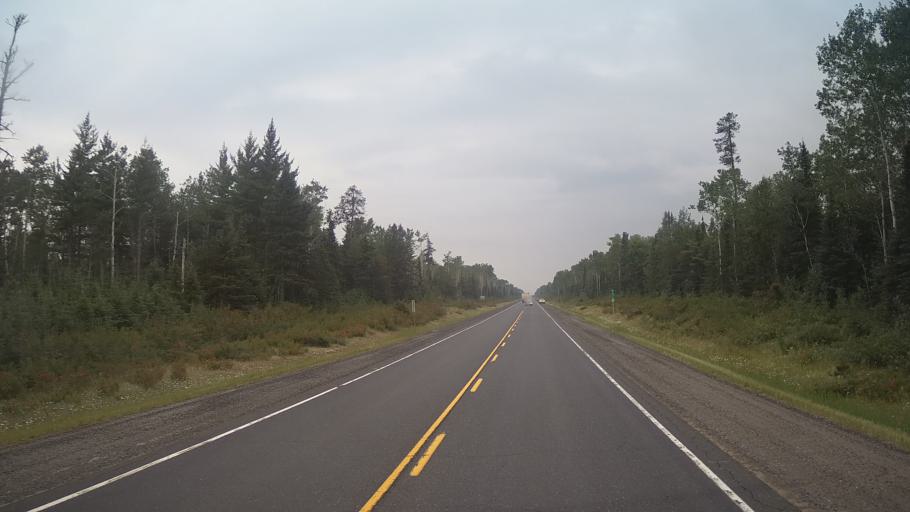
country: CA
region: Ontario
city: Greenstone
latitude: 49.2345
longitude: -88.1823
